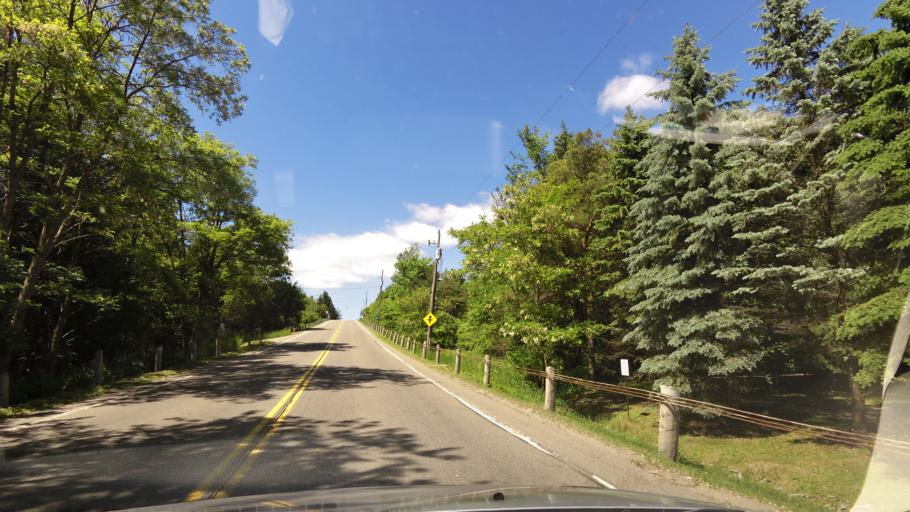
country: CA
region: Ontario
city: Newmarket
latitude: 43.9814
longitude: -79.5426
